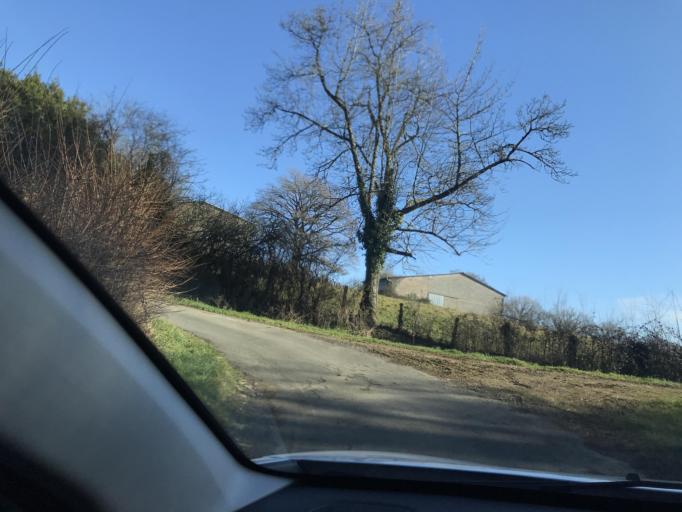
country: FR
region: Poitou-Charentes
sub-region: Departement de la Charente
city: Saint-Claud
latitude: 45.8515
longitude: 0.5239
